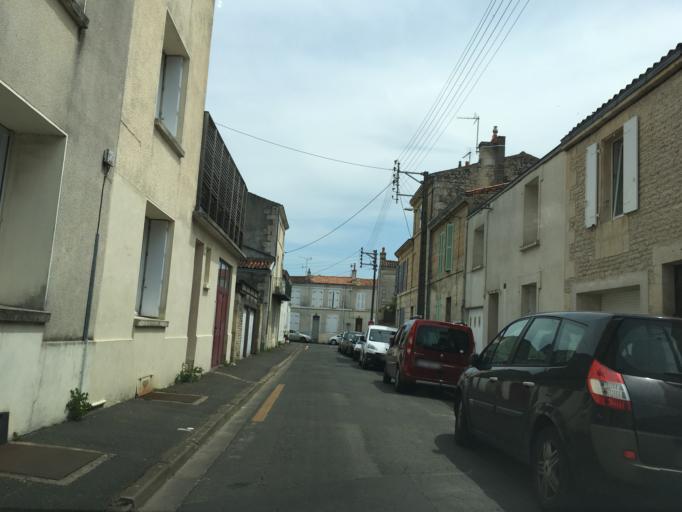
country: FR
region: Poitou-Charentes
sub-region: Departement des Deux-Sevres
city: Niort
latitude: 46.3211
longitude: -0.4724
